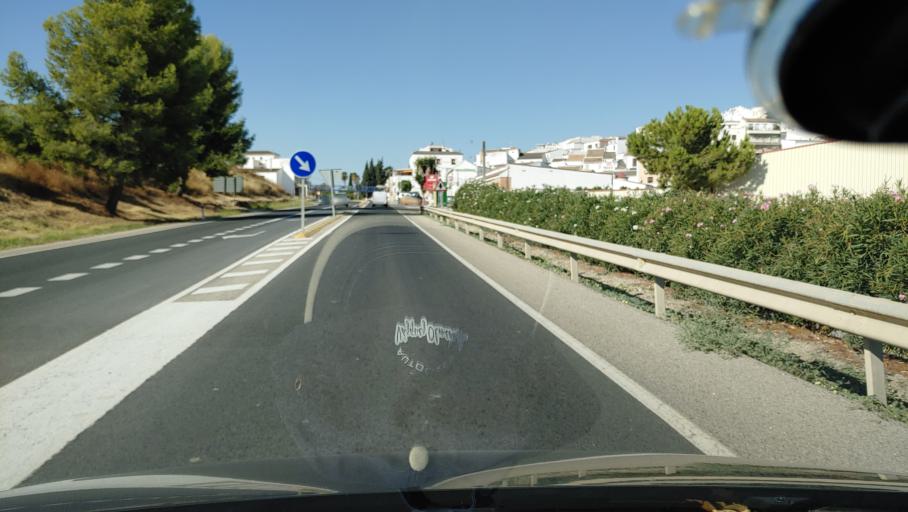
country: ES
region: Andalusia
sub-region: Province of Cordoba
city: Espejo
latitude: 37.6811
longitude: -4.5488
